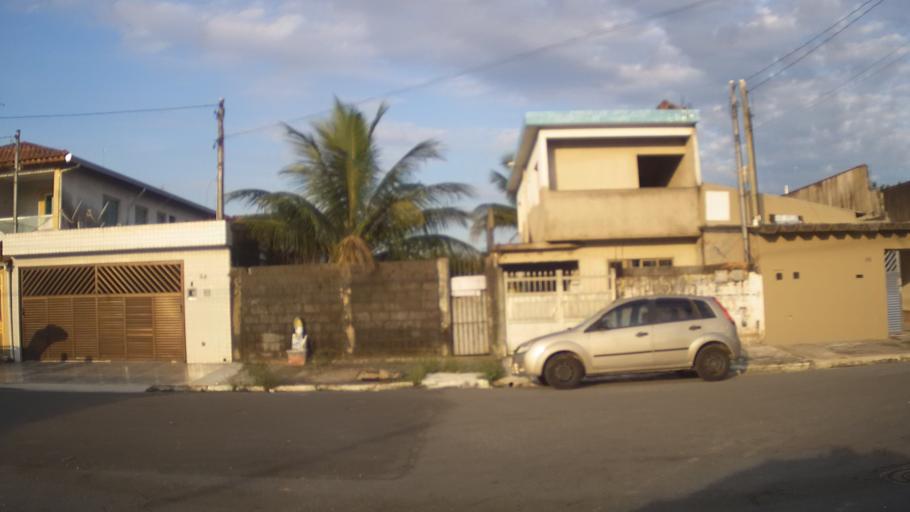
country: BR
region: Sao Paulo
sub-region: Praia Grande
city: Praia Grande
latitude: -23.9955
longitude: -46.4261
